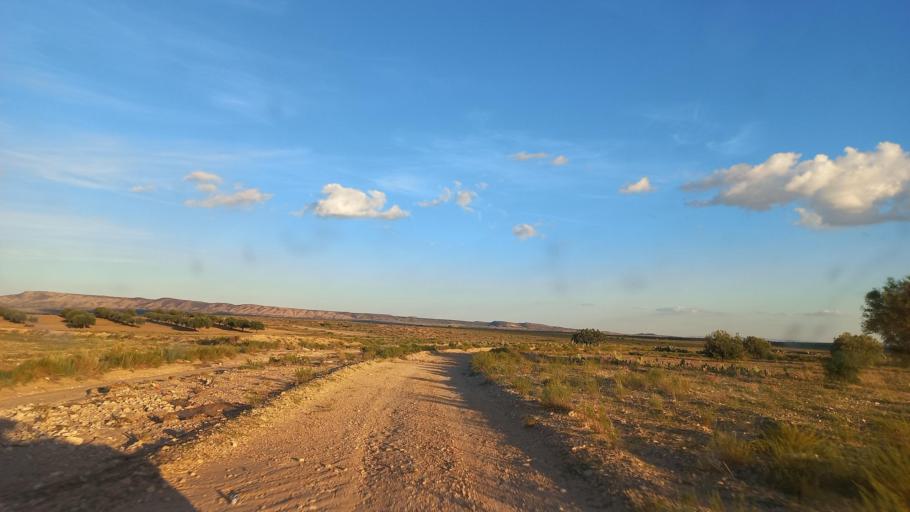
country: TN
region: Al Qasrayn
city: Sbiba
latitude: 35.3483
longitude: 9.0259
